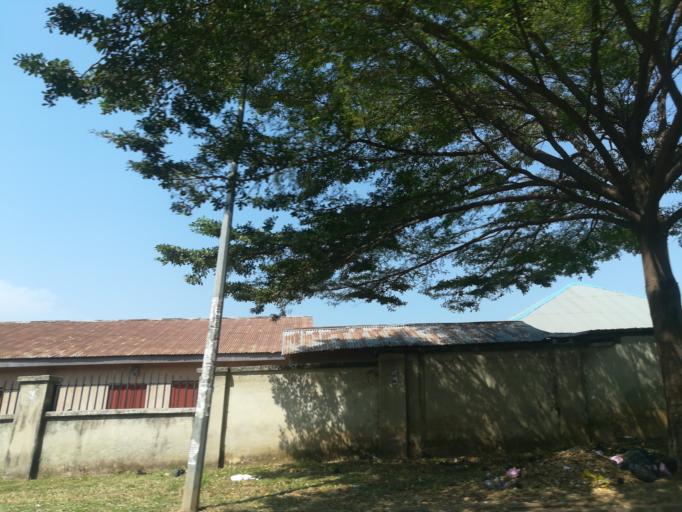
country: NG
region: Abuja Federal Capital Territory
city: Abuja
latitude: 9.0700
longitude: 7.4469
